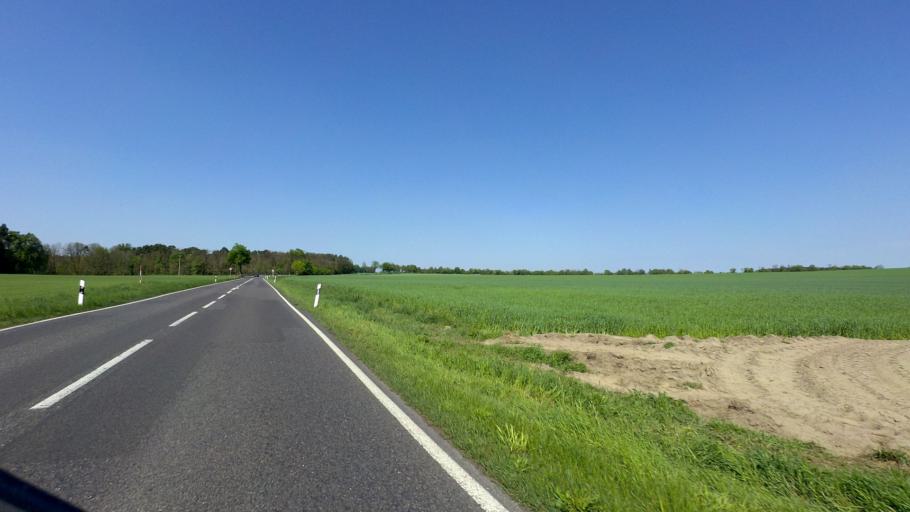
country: DE
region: Brandenburg
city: Friedland
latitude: 52.0895
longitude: 14.2586
